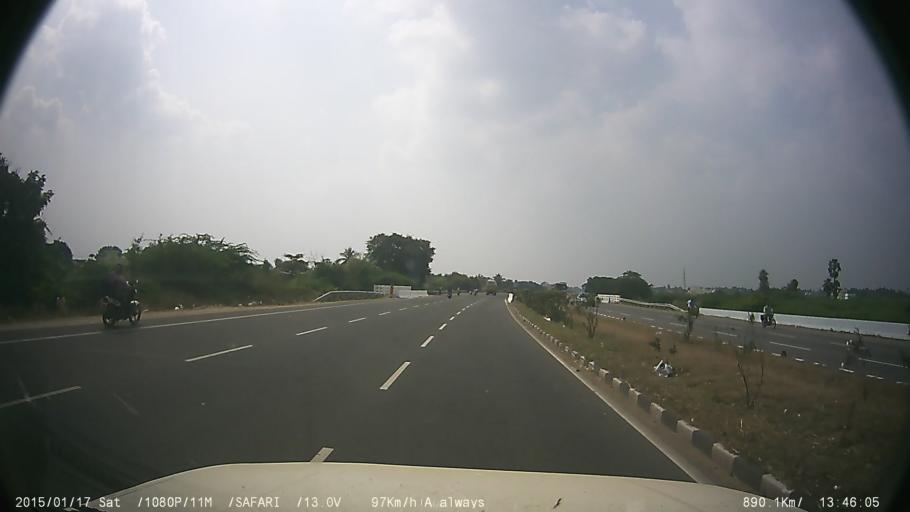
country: IN
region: Tamil Nadu
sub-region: Vellore
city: Vellore
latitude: 12.9149
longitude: 79.0854
